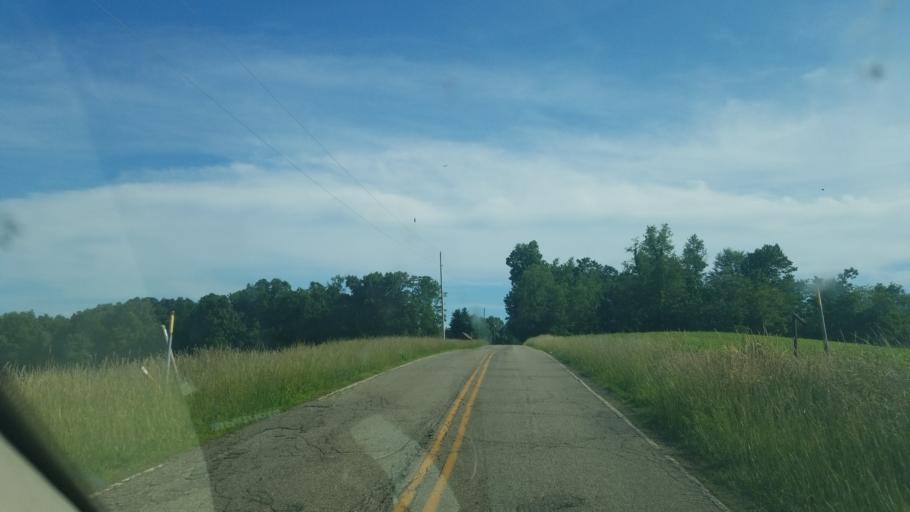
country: US
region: Ohio
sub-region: Holmes County
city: Millersburg
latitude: 40.4388
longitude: -81.9511
